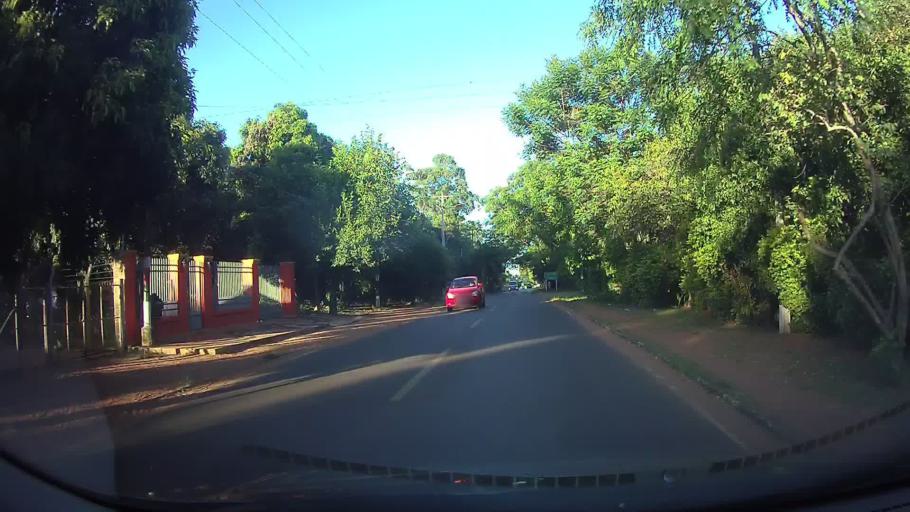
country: PY
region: Central
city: Aregua
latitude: -25.2944
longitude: -57.4135
